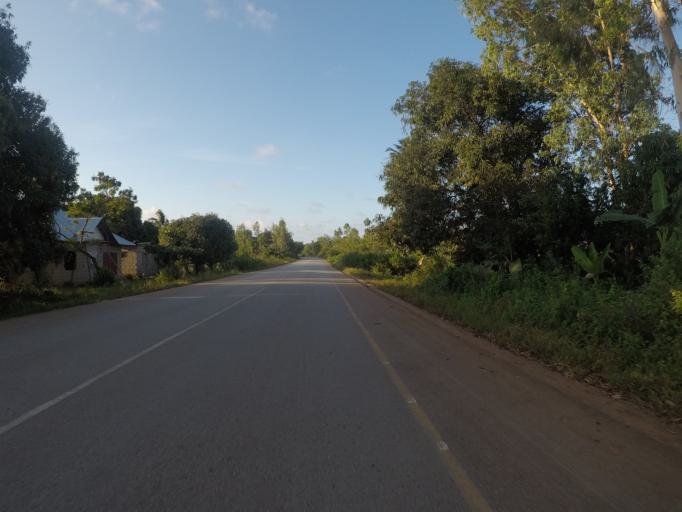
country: TZ
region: Zanzibar North
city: Kijini
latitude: -5.8510
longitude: 39.2831
